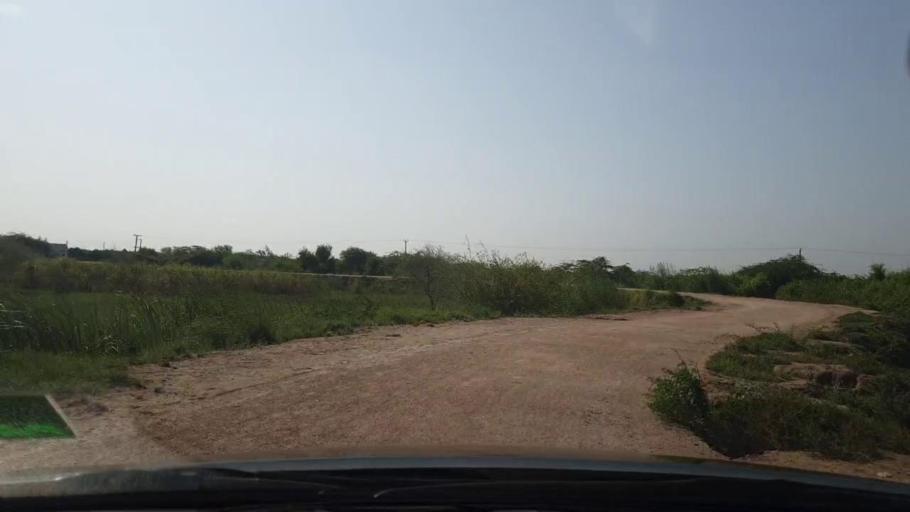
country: PK
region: Sindh
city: Tando Bago
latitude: 24.6966
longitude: 69.0205
